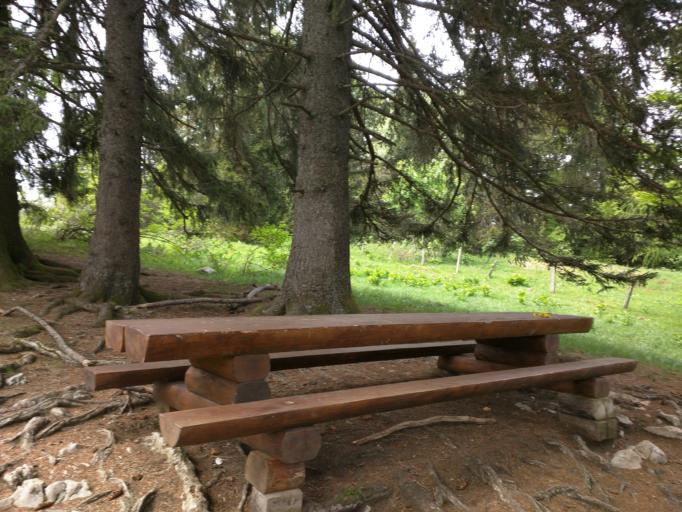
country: CH
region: Neuchatel
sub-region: Val-de-Ruz District
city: Les Geneveys-sur-Coffrane
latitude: 47.0284
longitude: 6.8135
